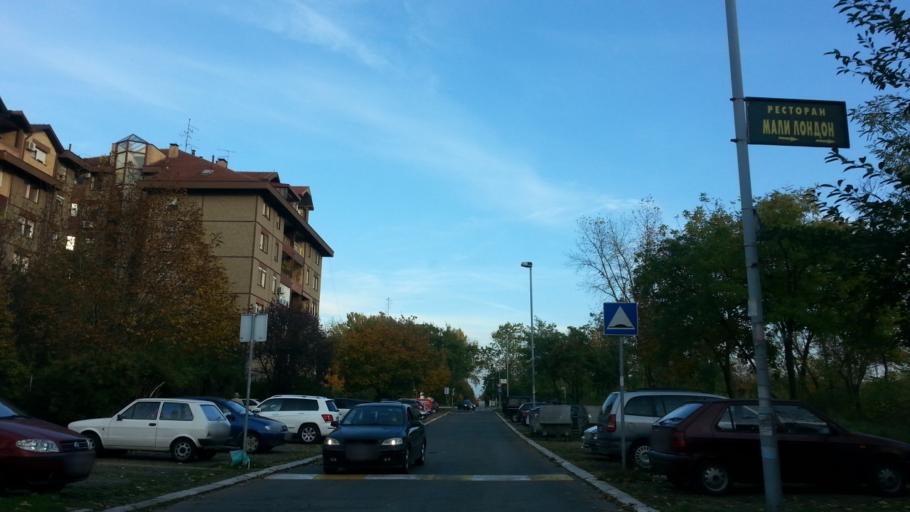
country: RS
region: Central Serbia
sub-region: Belgrade
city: Zemun
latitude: 44.8179
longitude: 20.3751
